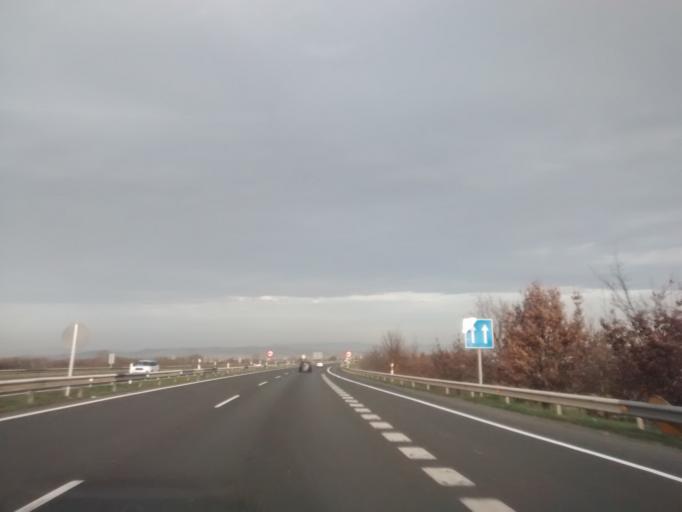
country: ES
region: Basque Country
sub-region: Provincia de Alava
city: Gasteiz / Vitoria
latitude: 42.8644
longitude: -2.7345
